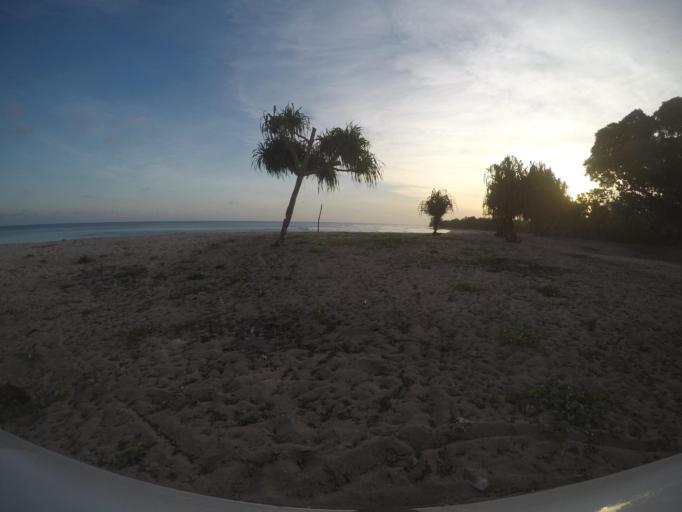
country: TL
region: Viqueque
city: Viqueque
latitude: -8.9470
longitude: 126.4497
